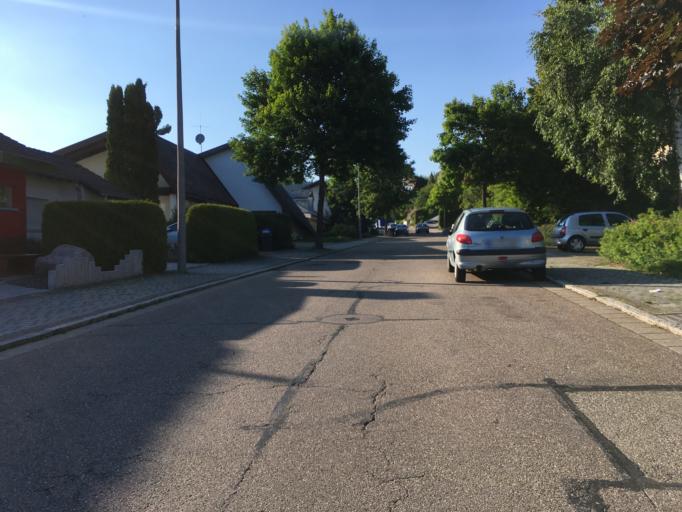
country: DE
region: Baden-Wuerttemberg
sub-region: Freiburg Region
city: Titisee-Neustadt
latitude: 47.9161
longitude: 8.2210
